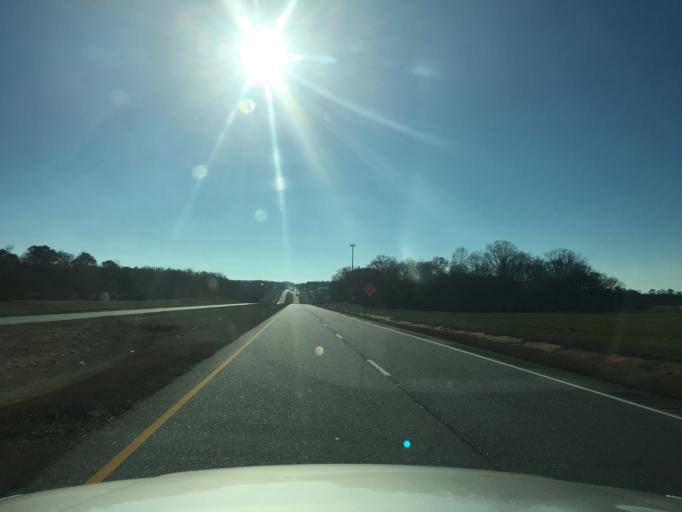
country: US
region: Georgia
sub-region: Carroll County
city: Carrollton
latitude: 33.4834
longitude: -85.0991
